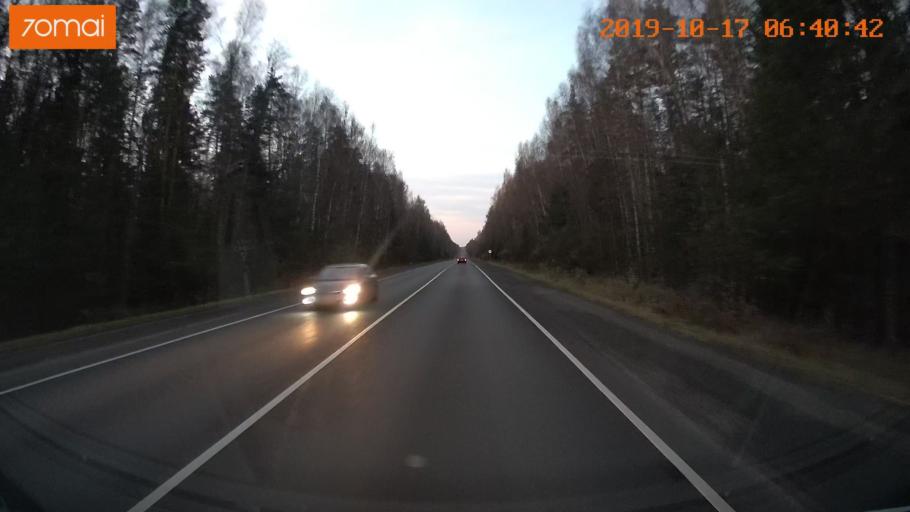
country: RU
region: Ivanovo
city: Nerl'
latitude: 56.6253
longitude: 40.5670
